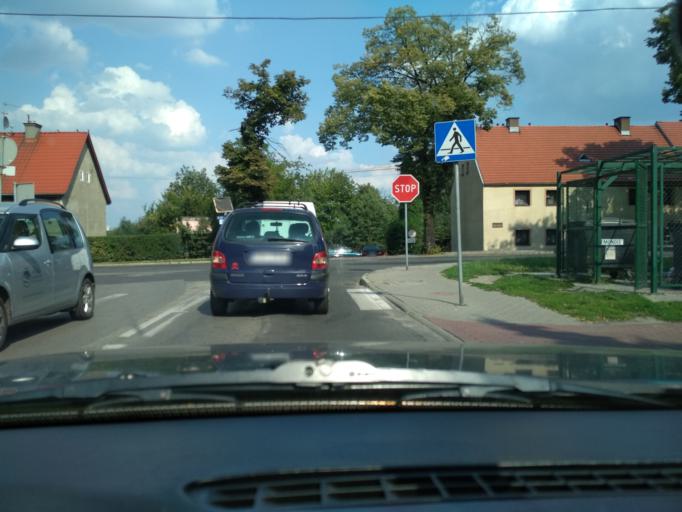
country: PL
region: Silesian Voivodeship
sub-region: Gliwice
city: Gliwice
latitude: 50.2764
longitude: 18.6737
